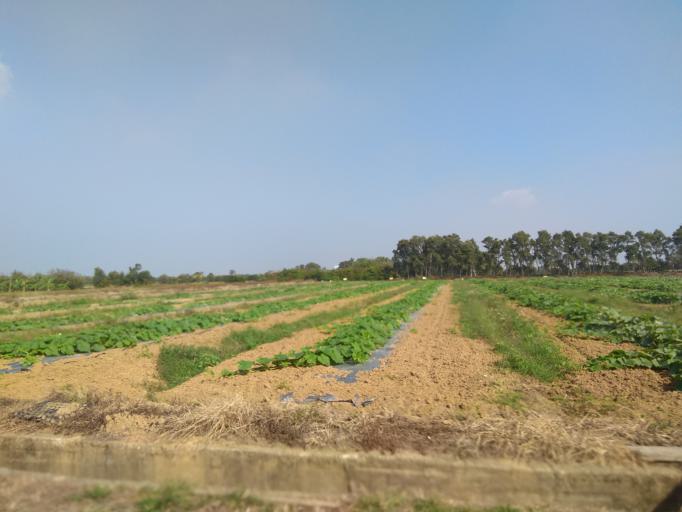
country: TW
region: Taiwan
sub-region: Hsinchu
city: Zhubei
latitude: 24.9962
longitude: 121.0630
